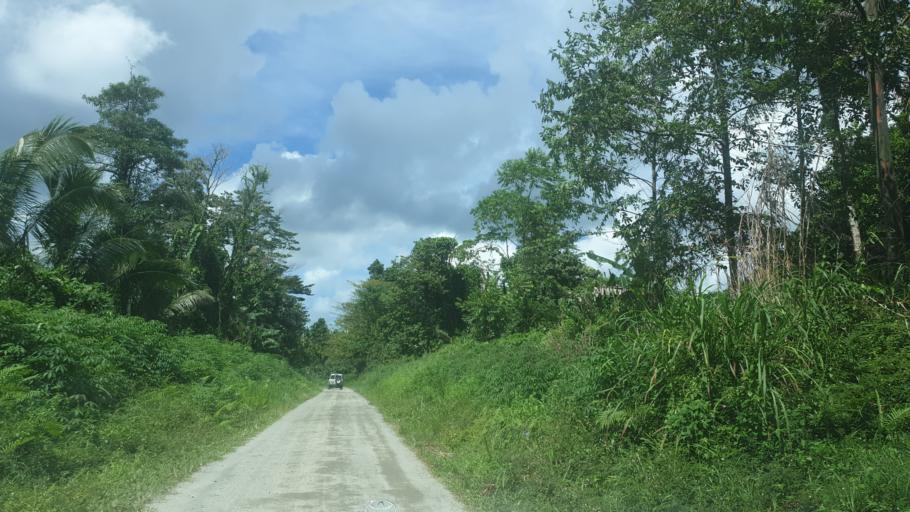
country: PG
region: Bougainville
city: Panguna
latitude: -6.7321
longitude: 155.4918
